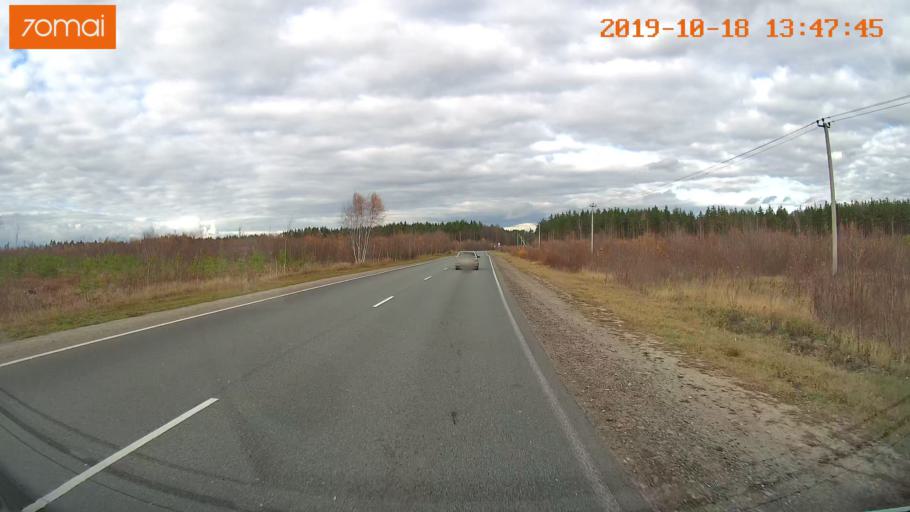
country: RU
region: Moskovskaya
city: Radovitskiy
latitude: 54.9796
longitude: 39.9515
